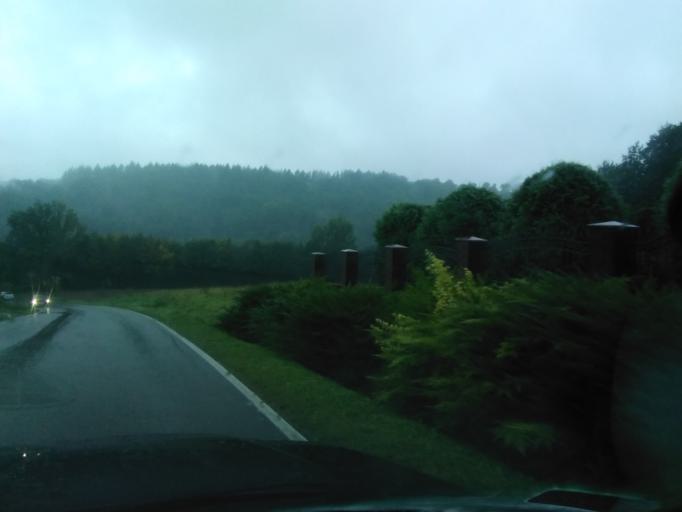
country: PL
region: Subcarpathian Voivodeship
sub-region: Powiat ropczycko-sedziszowski
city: Niedzwiada
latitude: 50.0377
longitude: 21.5443
